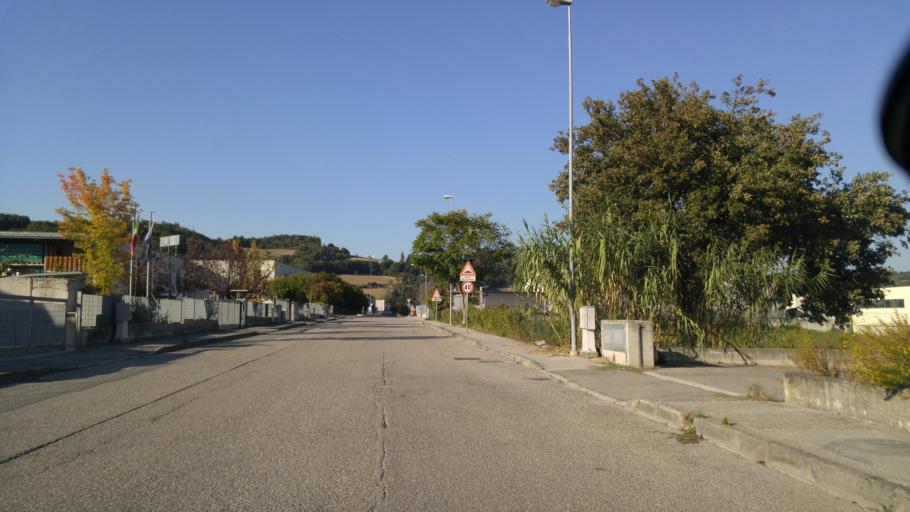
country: IT
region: The Marches
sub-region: Provincia di Pesaro e Urbino
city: Fermignano
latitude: 43.6888
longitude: 12.6483
